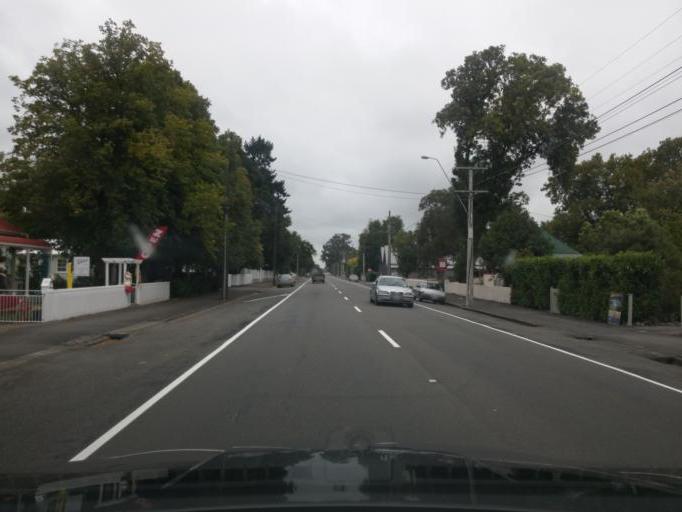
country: NZ
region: Wellington
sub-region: Masterton District
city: Masterton
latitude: -41.0858
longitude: 175.4543
